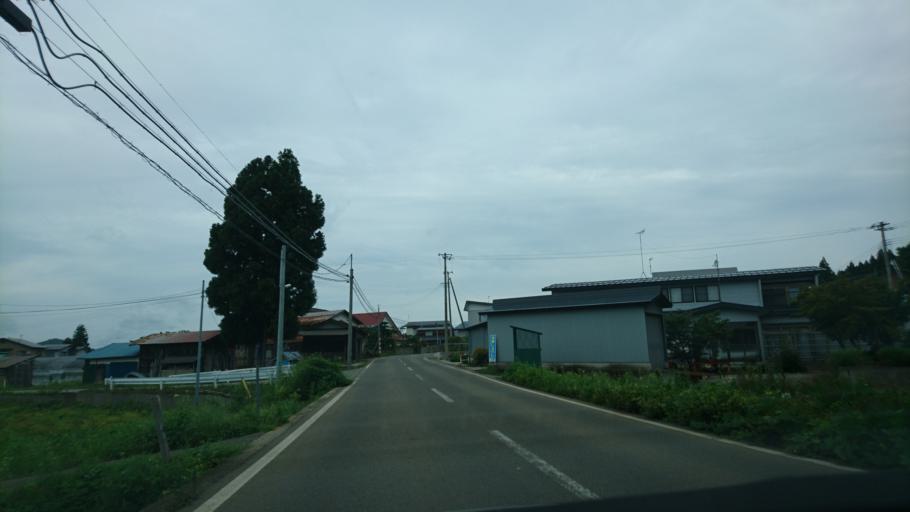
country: JP
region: Akita
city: Yuzawa
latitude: 39.1425
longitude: 140.5768
